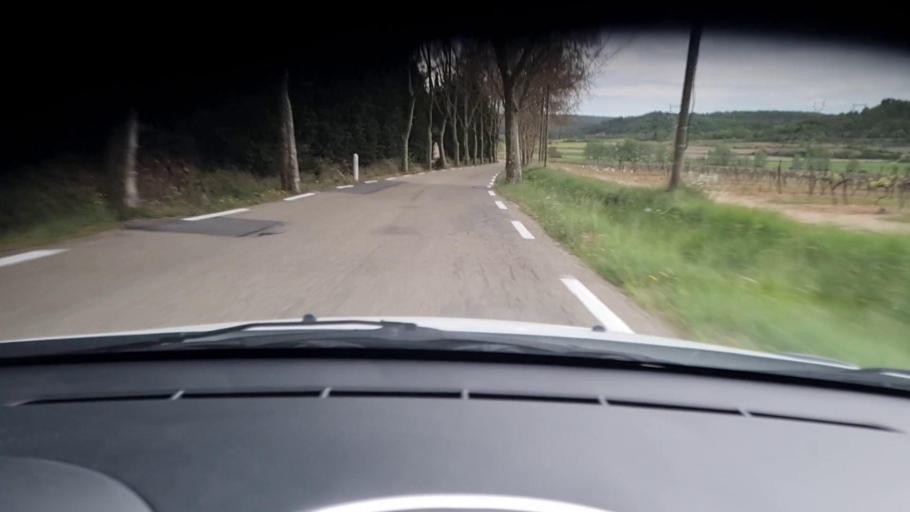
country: FR
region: Languedoc-Roussillon
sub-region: Departement du Gard
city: Blauzac
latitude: 43.9608
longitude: 4.3841
